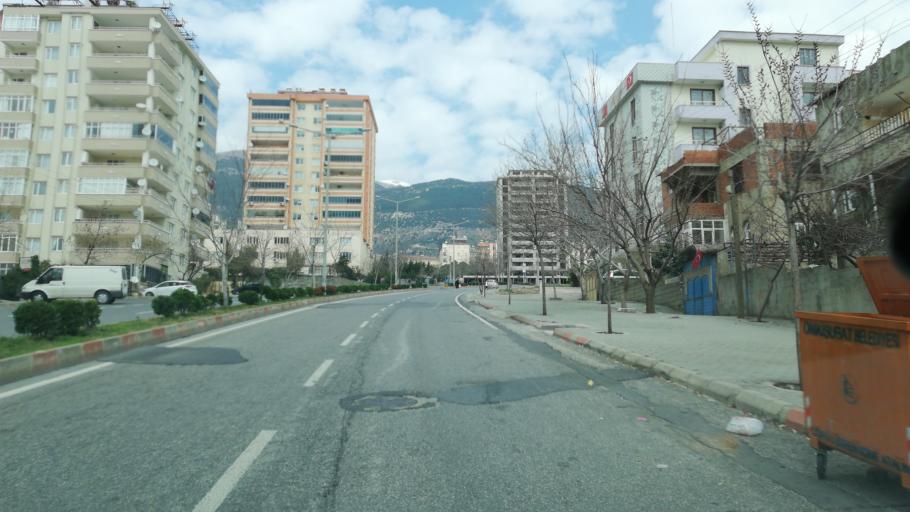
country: TR
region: Kahramanmaras
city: Kahramanmaras
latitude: 37.5908
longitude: 36.8634
